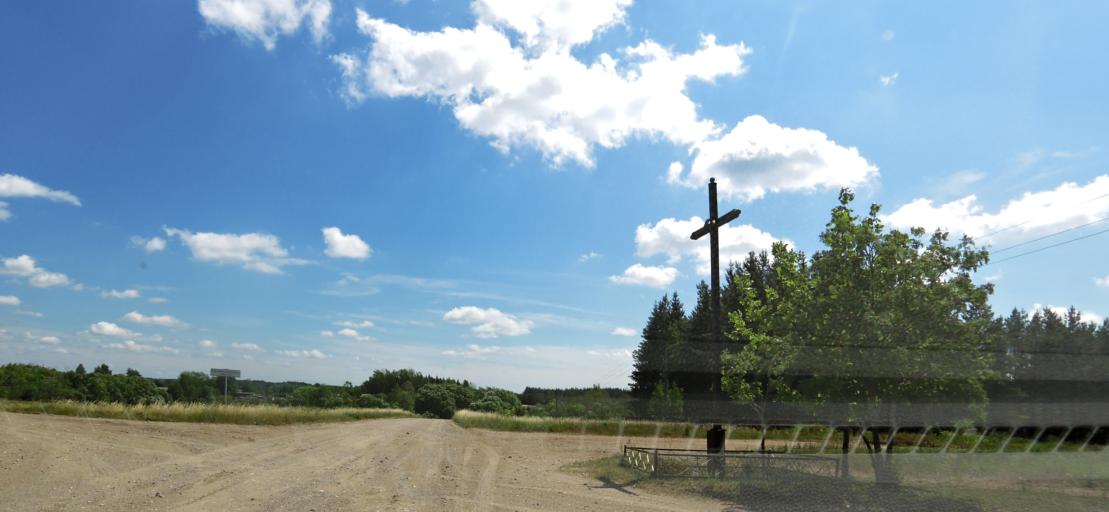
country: LT
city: Nemencine
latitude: 54.8700
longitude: 25.5345
